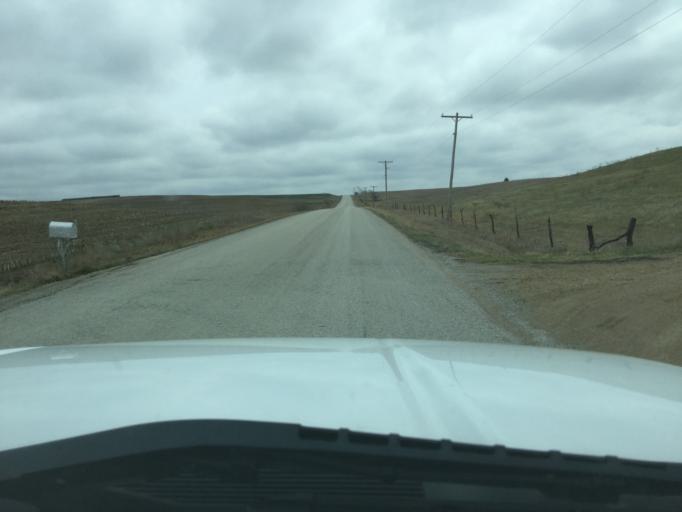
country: US
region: Kansas
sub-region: Nemaha County
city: Seneca
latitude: 39.7400
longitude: -96.0293
